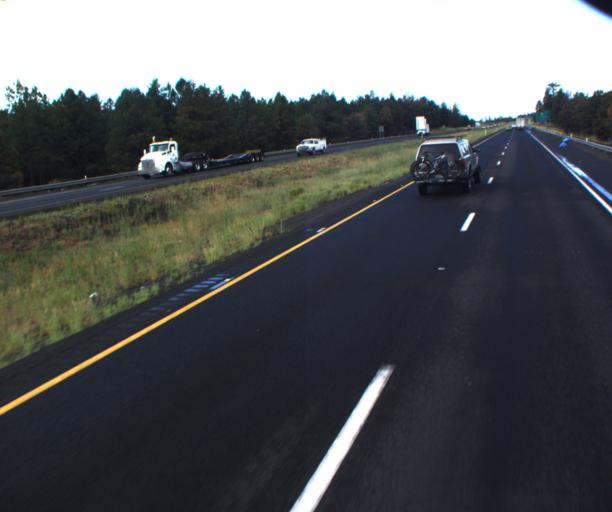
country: US
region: Arizona
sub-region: Coconino County
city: Flagstaff
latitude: 35.1530
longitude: -111.6807
